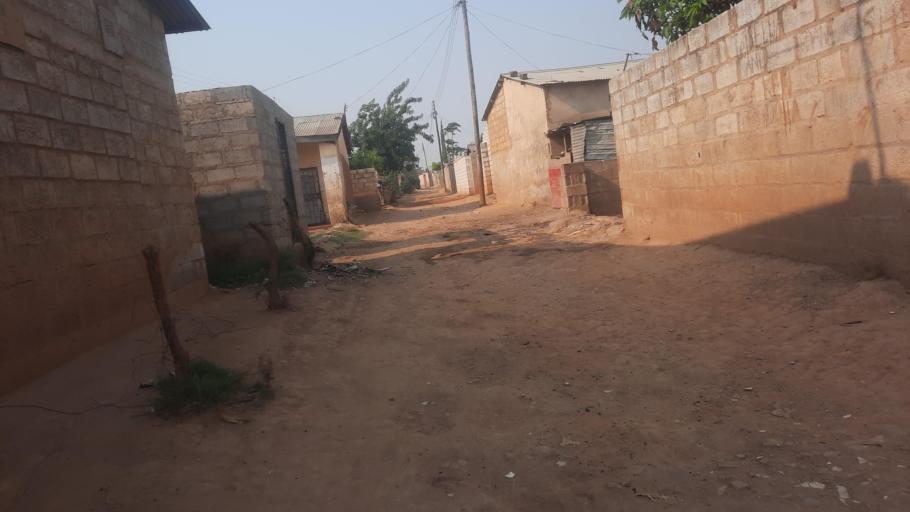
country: ZM
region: Lusaka
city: Lusaka
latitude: -15.3952
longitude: 28.3838
